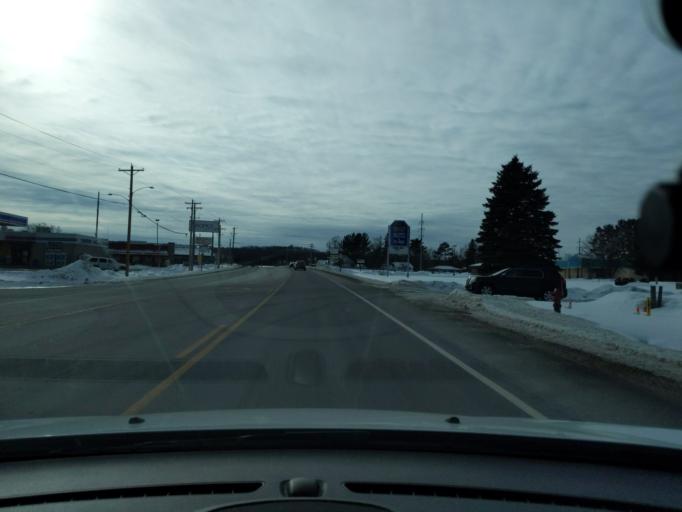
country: US
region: Wisconsin
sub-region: Washburn County
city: Spooner
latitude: 45.8161
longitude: -91.8963
